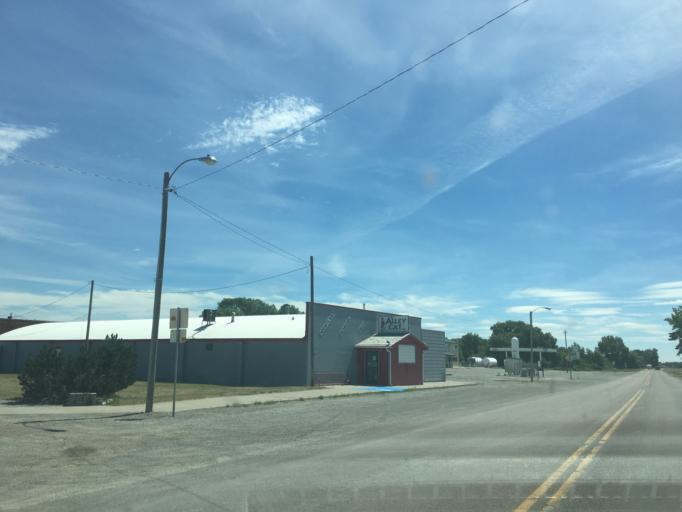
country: US
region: Montana
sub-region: Teton County
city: Choteau
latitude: 47.8069
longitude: -112.1789
